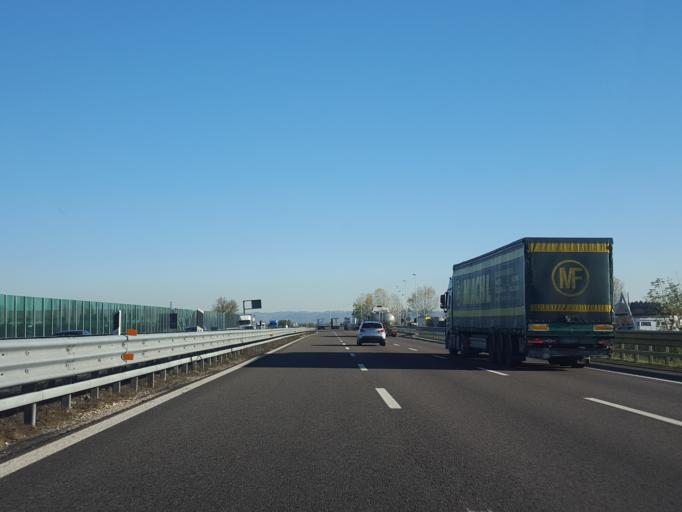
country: IT
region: Veneto
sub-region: Provincia di Verona
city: Soave
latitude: 45.4087
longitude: 11.2652
